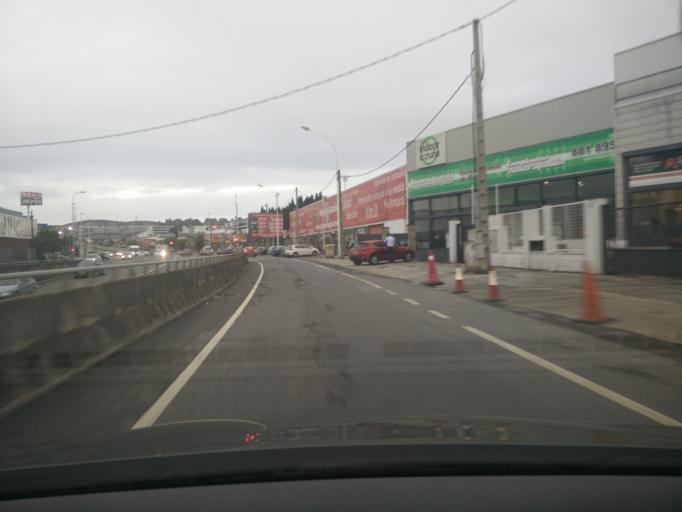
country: ES
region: Galicia
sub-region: Provincia da Coruna
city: A Coruna
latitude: 43.3499
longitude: -8.4214
